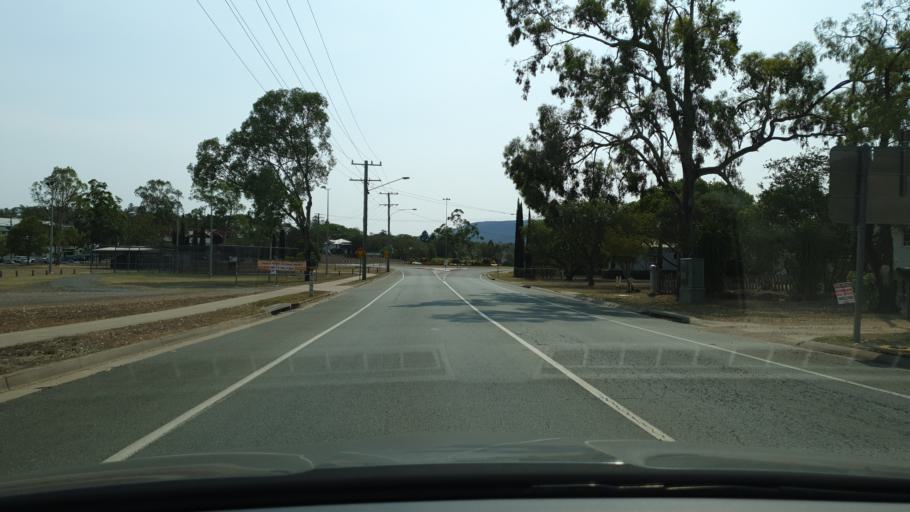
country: AU
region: Queensland
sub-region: Ipswich
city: Deebing Heights
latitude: -27.9933
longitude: 152.6842
